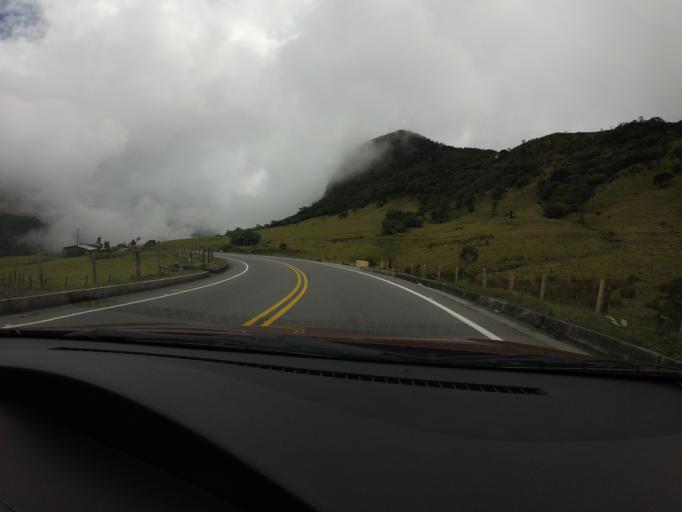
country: CO
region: Tolima
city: Herveo
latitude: 5.0342
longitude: -75.3339
